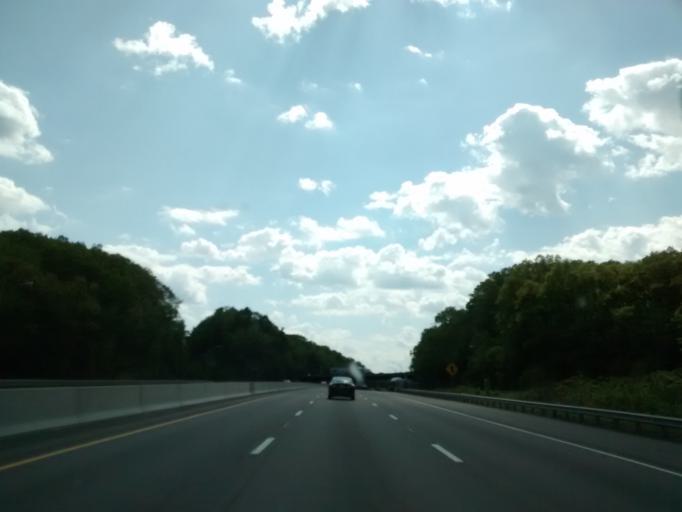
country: US
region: Massachusetts
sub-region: Worcester County
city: Auburn
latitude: 42.1938
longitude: -71.8497
